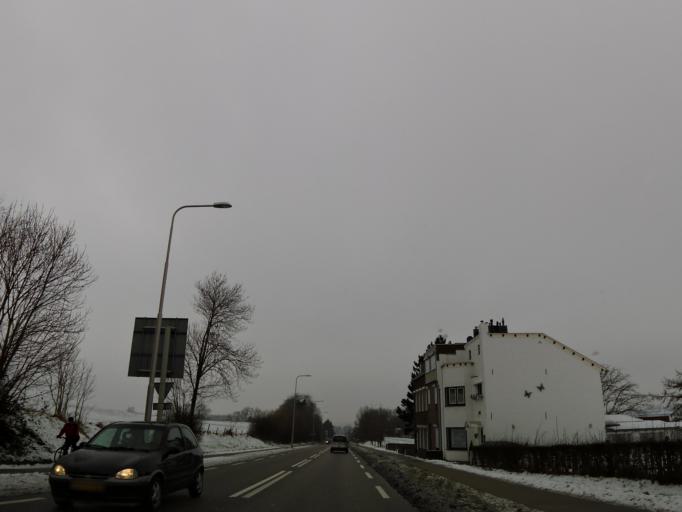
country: NL
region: Limburg
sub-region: Gemeente Vaals
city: Vaals
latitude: 50.7784
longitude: 6.0056
